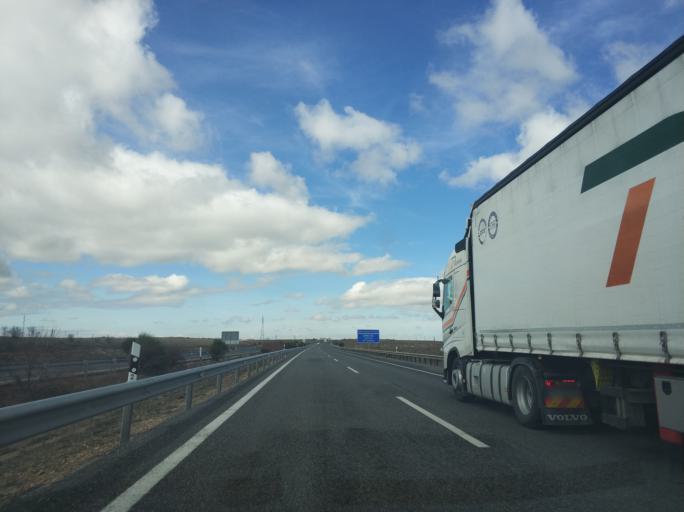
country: ES
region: Castille and Leon
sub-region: Provincia de Burgos
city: Villagonzalo-Pedernales
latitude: 42.3038
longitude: -3.7639
